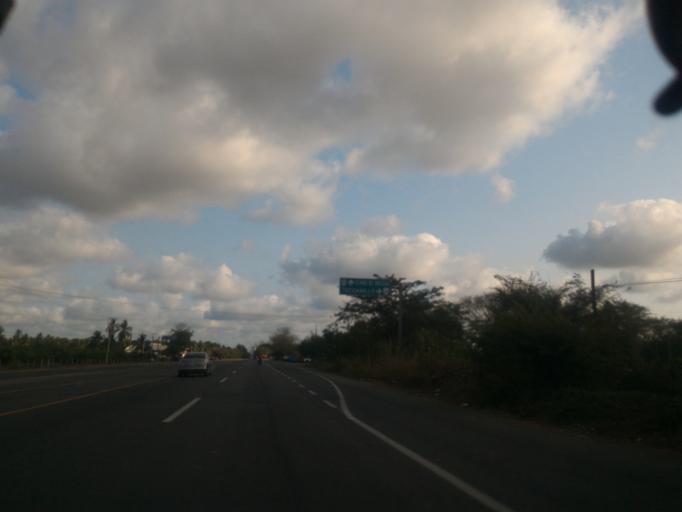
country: MX
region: Colima
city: Tecoman
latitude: 18.8918
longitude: -103.8556
